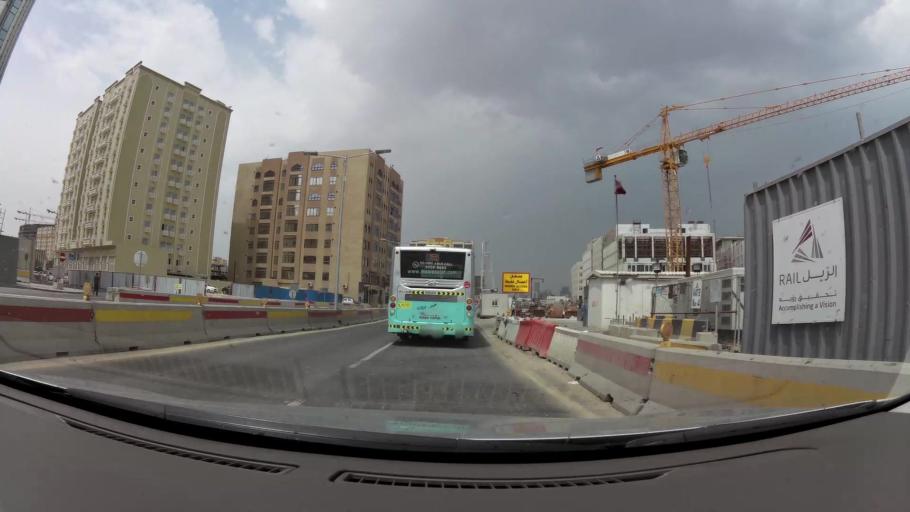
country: QA
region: Baladiyat ad Dawhah
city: Doha
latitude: 25.2831
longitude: 51.5241
